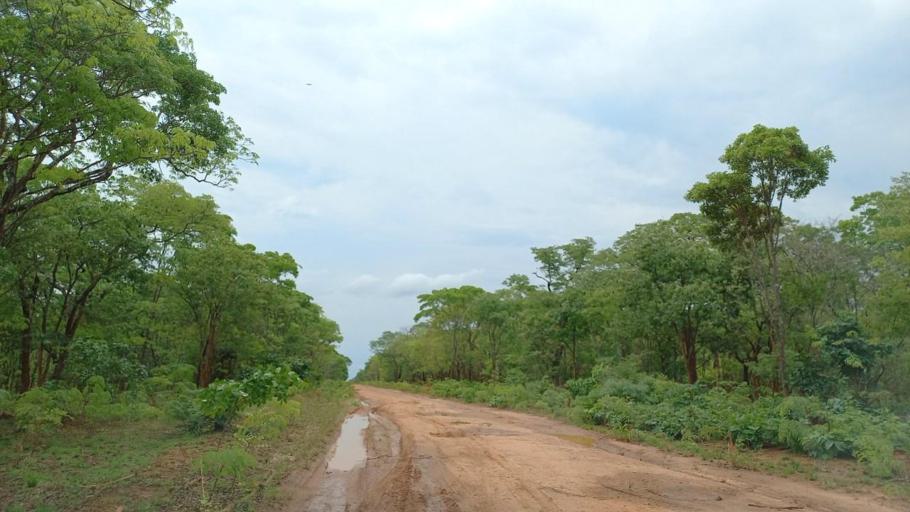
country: ZM
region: North-Western
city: Kalengwa
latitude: -13.6088
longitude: 24.9752
